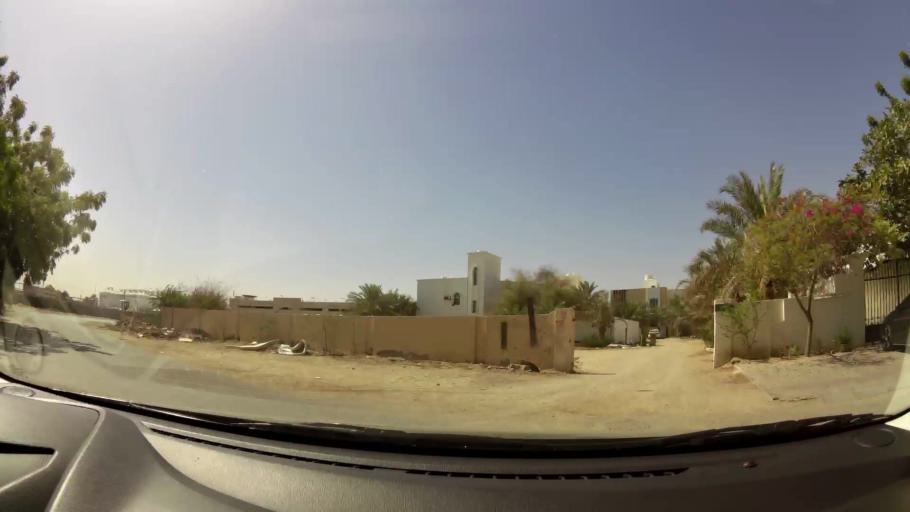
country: OM
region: Muhafazat Masqat
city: As Sib al Jadidah
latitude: 23.6032
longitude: 58.2465
